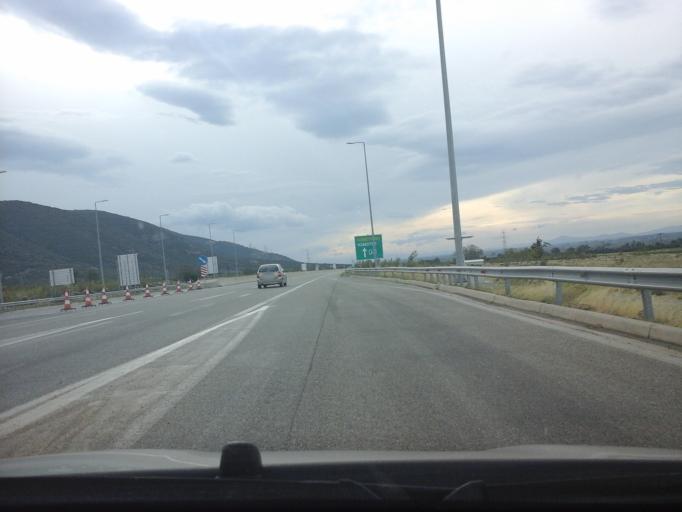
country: GR
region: East Macedonia and Thrace
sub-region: Nomos Xanthis
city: Selero
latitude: 41.1203
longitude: 25.0802
